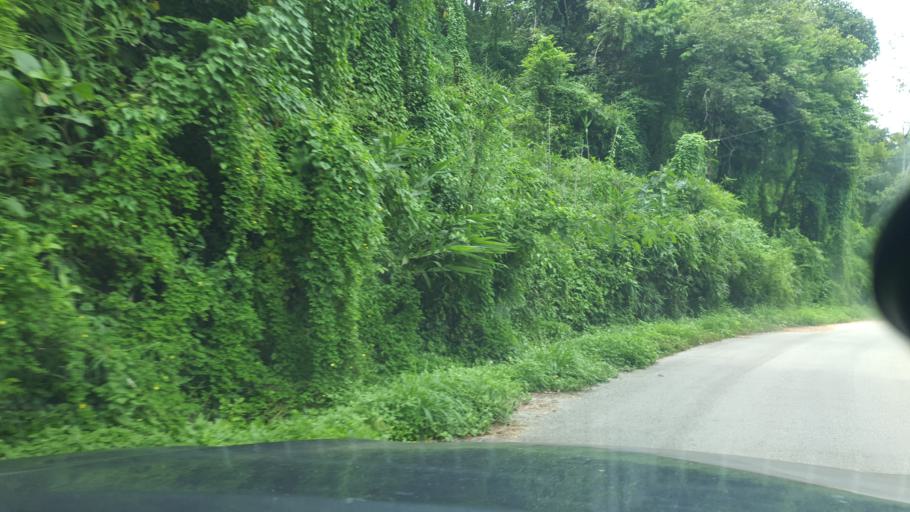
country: TH
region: Lampang
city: Hang Chat
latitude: 18.4196
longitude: 99.2631
